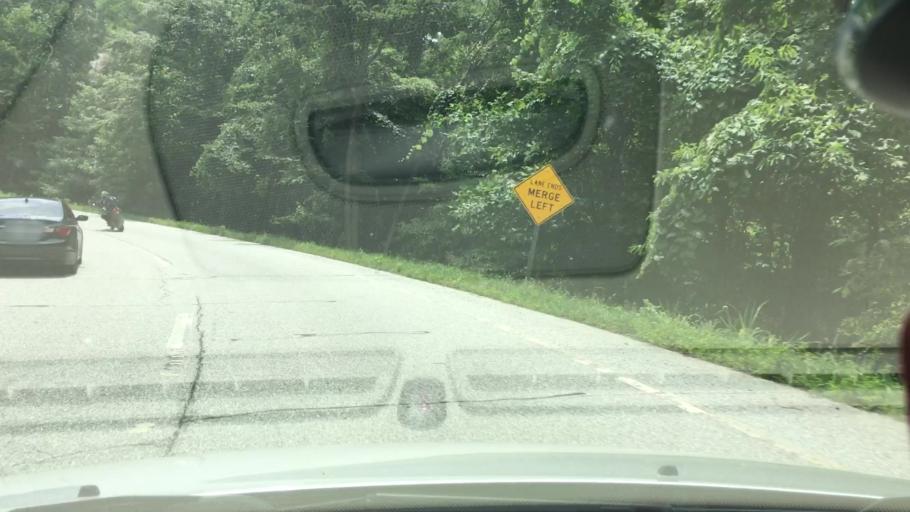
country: US
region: Georgia
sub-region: Union County
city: Blairsville
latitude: 34.7553
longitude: -83.9253
